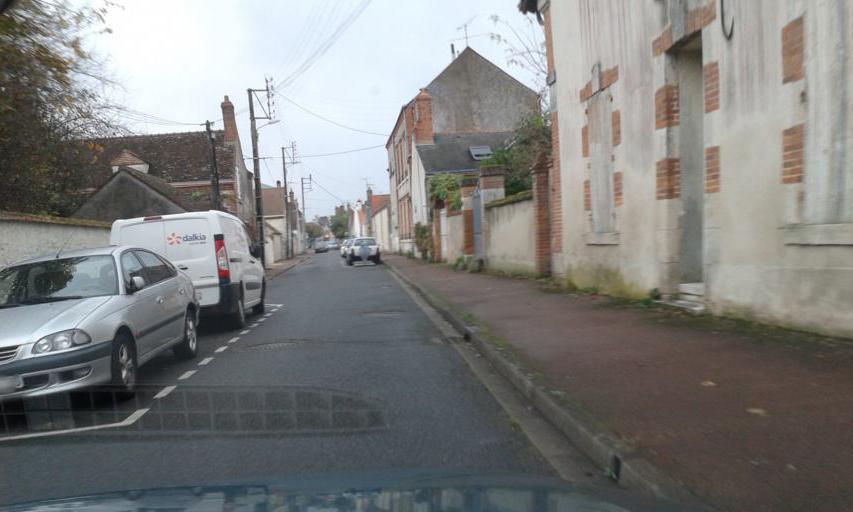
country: FR
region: Centre
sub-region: Departement du Loiret
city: Olivet
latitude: 47.8601
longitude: 1.8997
